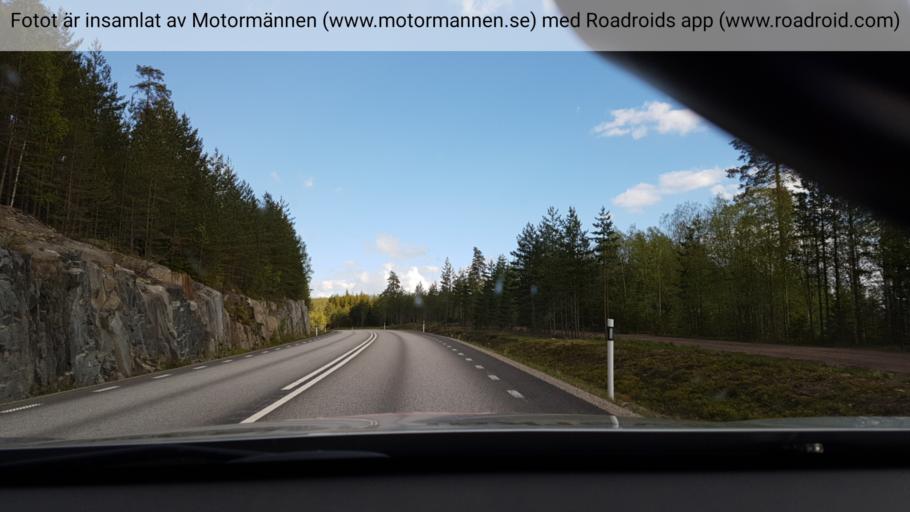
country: SE
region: Dalarna
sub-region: Faluns Kommun
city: Bjursas
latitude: 60.7892
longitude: 15.2816
